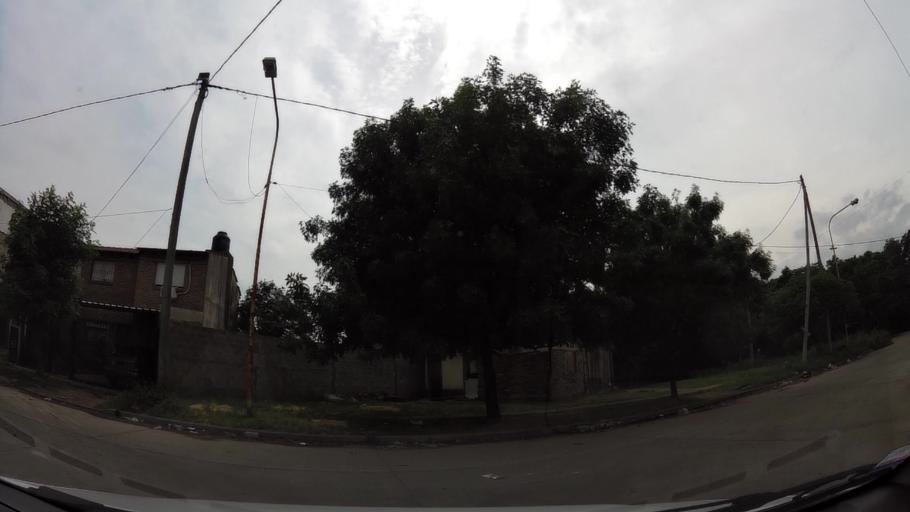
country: AR
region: Buenos Aires
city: San Justo
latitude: -34.6987
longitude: -58.5196
